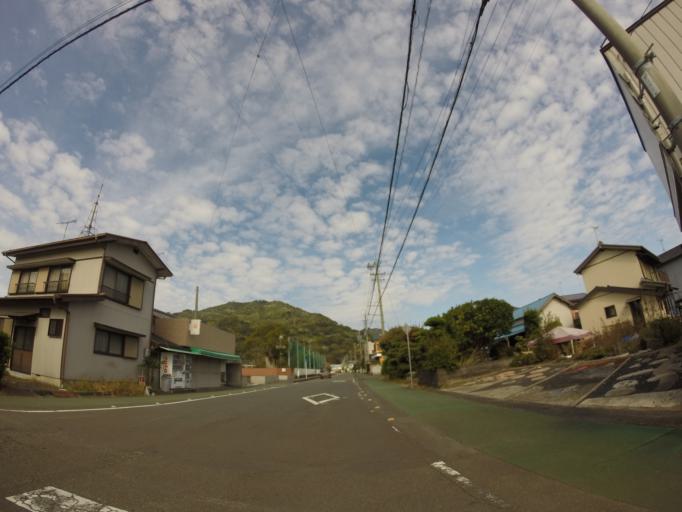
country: JP
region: Shizuoka
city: Yaizu
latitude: 34.8862
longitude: 138.3213
